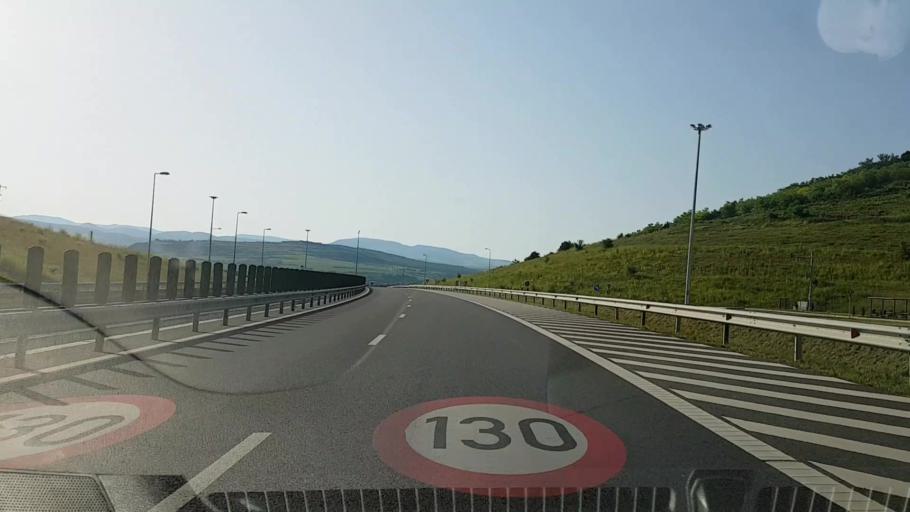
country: RO
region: Alba
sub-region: Comuna Miraslau
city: Miraslau
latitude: 46.3448
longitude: 23.7330
